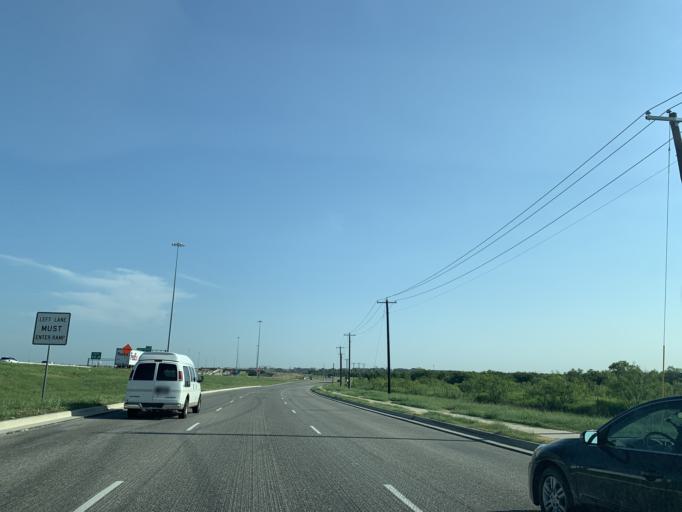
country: US
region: Texas
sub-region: Tarrant County
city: Blue Mound
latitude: 32.8772
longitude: -97.3166
